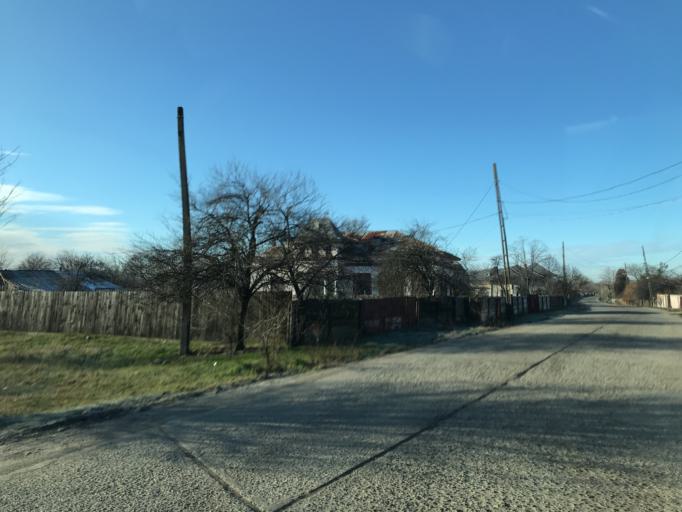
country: RO
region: Olt
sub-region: Comuna Piatra Olt
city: Piatra
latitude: 44.3754
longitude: 24.2845
